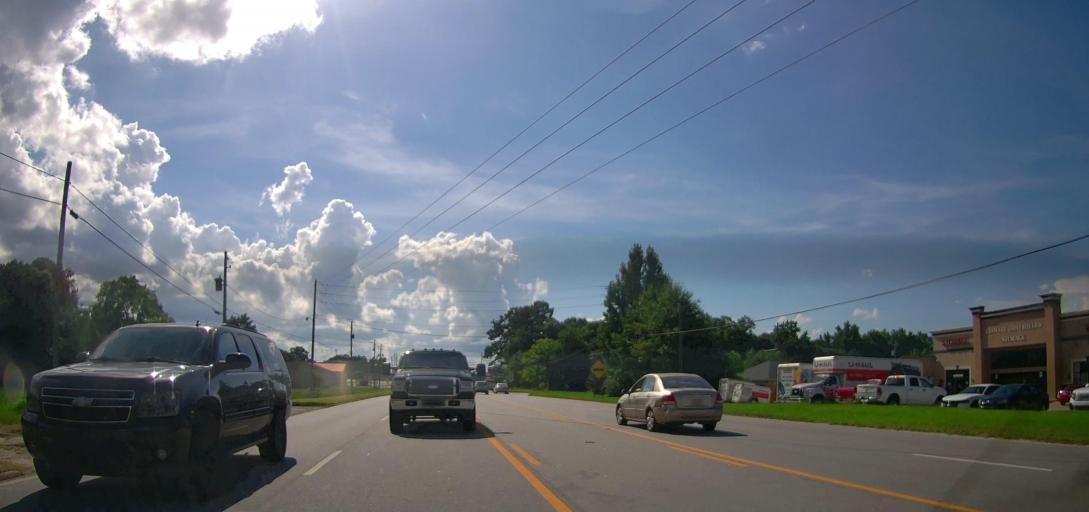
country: US
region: Alabama
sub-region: Russell County
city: Ladonia
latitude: 32.4687
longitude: -85.0808
